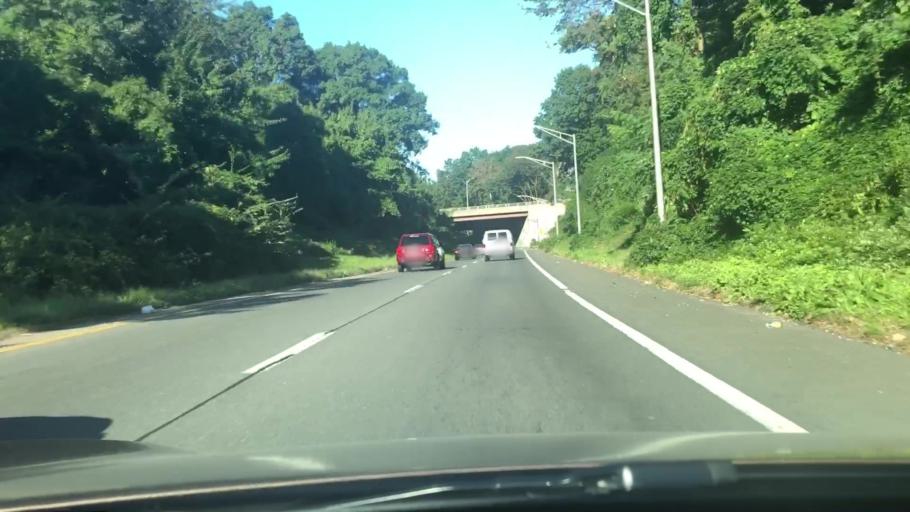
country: US
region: New York
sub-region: Westchester County
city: Pelham
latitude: 40.9222
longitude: -73.8140
